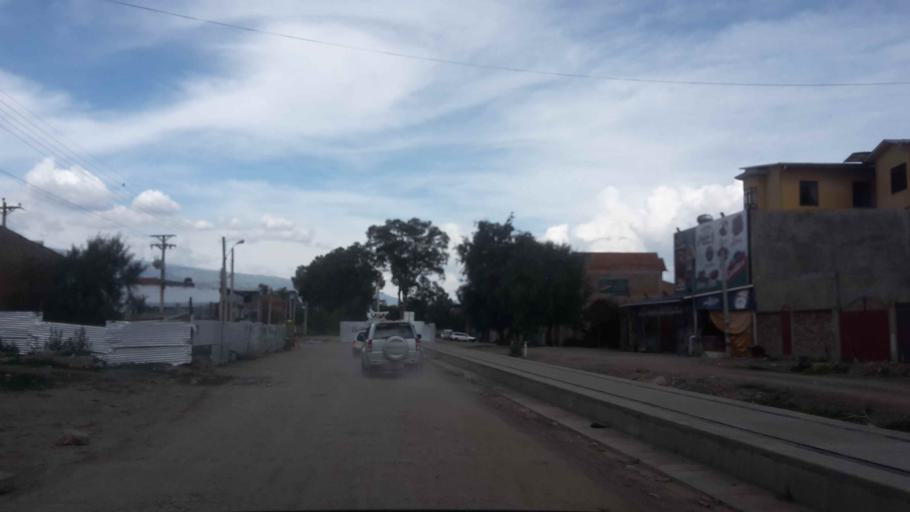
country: BO
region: Cochabamba
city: Sipe Sipe
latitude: -17.4012
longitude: -66.2754
